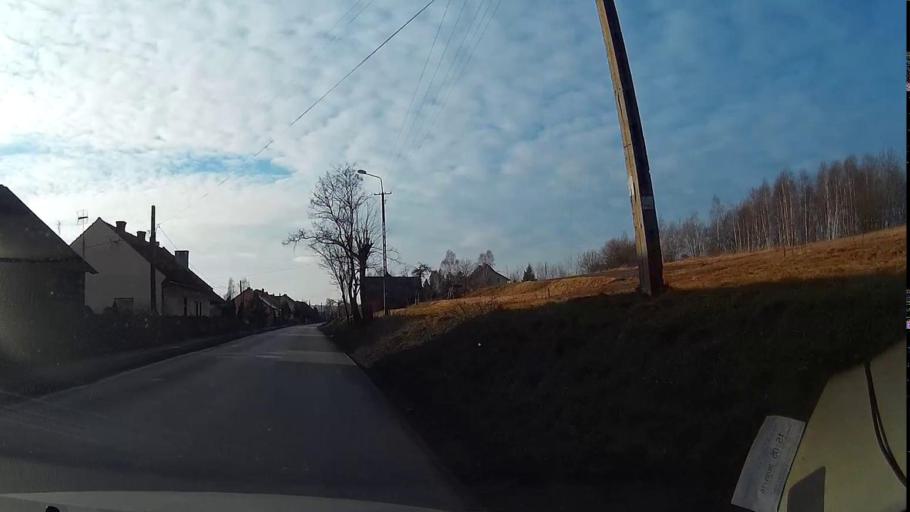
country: PL
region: Lesser Poland Voivodeship
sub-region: Powiat krakowski
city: Liszki
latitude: 50.0582
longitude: 19.7559
